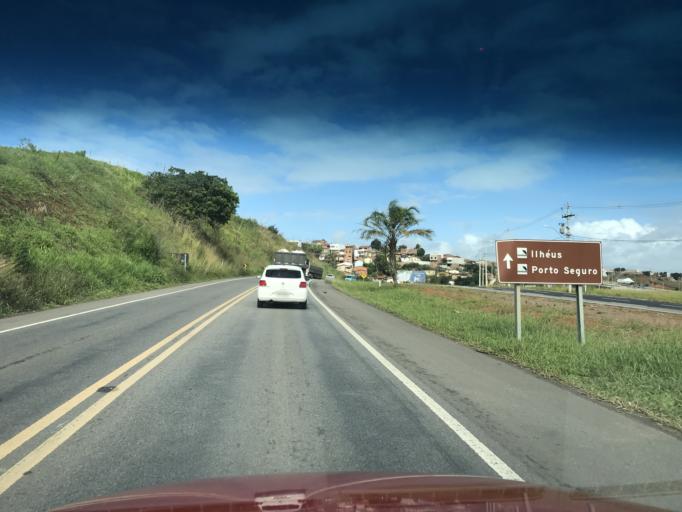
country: BR
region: Bahia
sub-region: Santo Antonio De Jesus
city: Santo Antonio de Jesus
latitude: -12.9543
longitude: -39.2566
